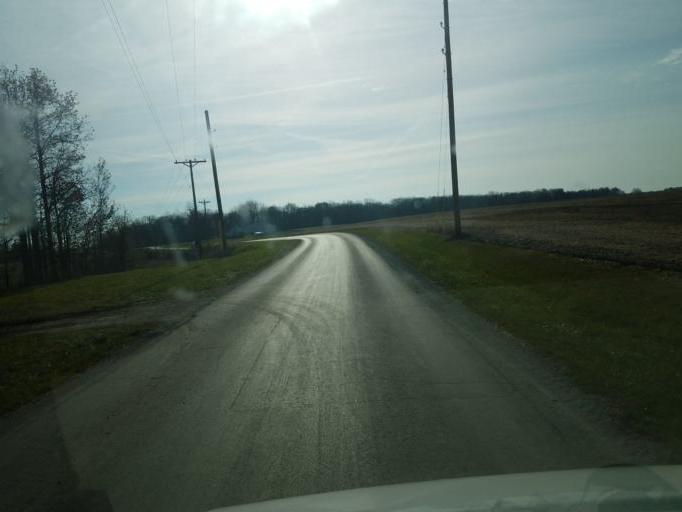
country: US
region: Ohio
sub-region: Hardin County
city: Kenton
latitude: 40.5829
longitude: -83.4543
